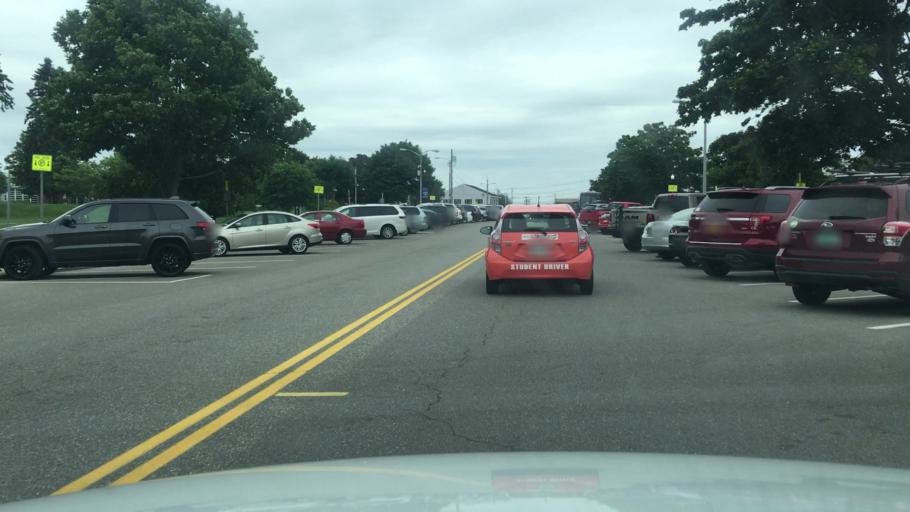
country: US
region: Maine
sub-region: York County
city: Old Orchard Beach
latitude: 43.5138
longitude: -70.3768
